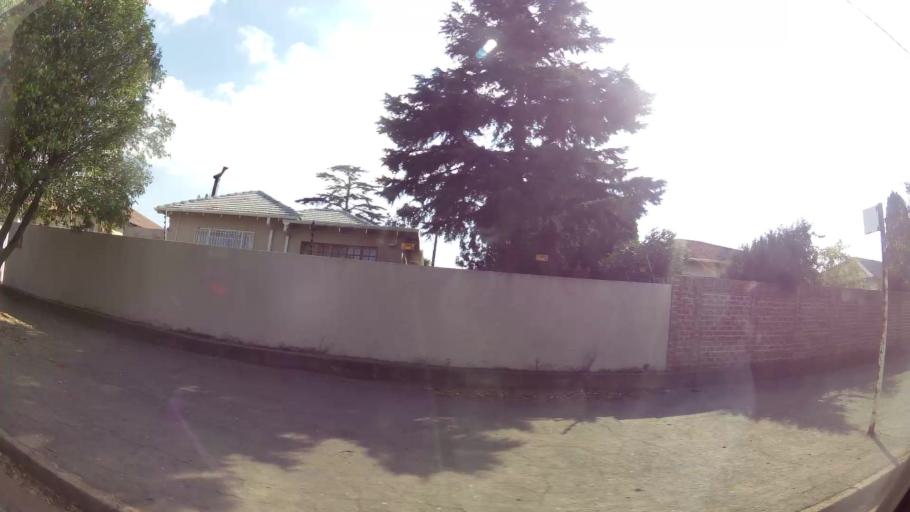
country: ZA
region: Gauteng
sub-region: Ekurhuleni Metropolitan Municipality
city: Germiston
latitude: -26.1765
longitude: 28.1784
